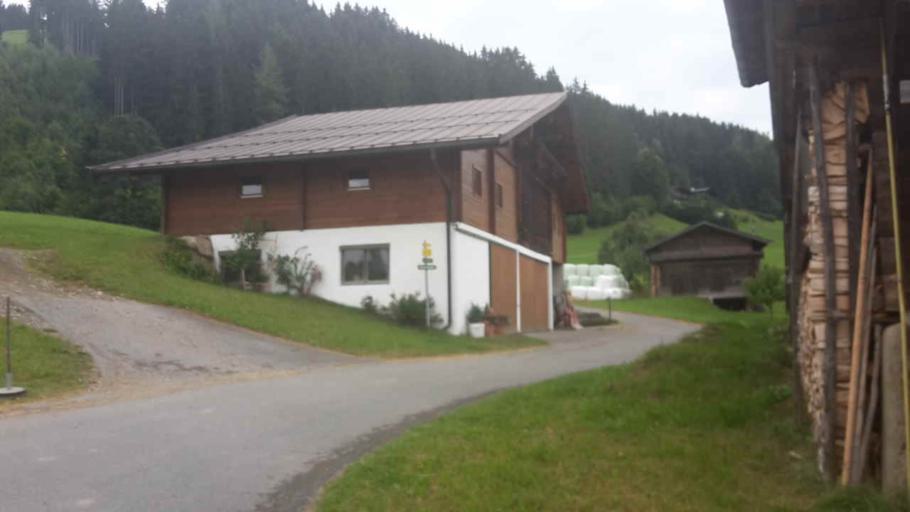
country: AT
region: Tyrol
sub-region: Politischer Bezirk Kitzbuhel
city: Kirchberg in Tirol
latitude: 47.4378
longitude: 12.3257
